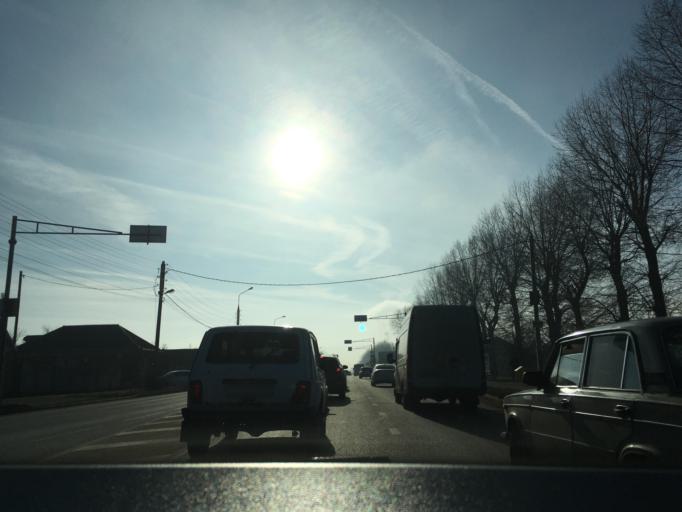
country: RU
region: Krasnodarskiy
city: Krasnodar
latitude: 45.1057
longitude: 39.0127
